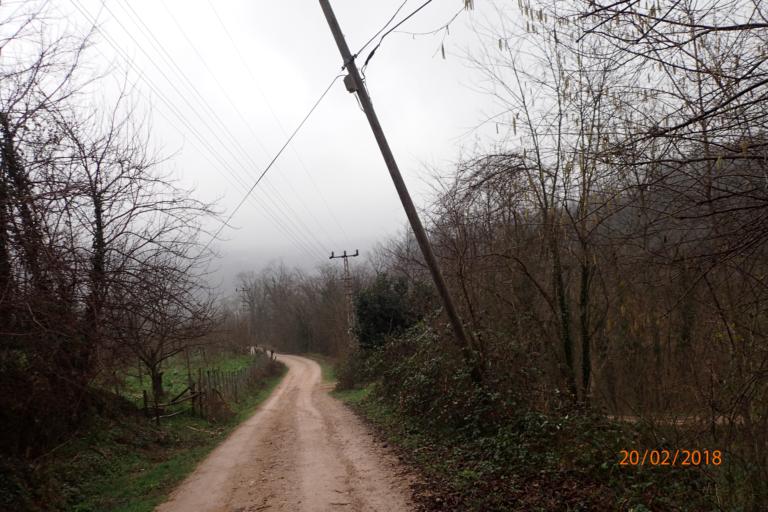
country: TR
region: Ordu
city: Camas
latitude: 40.9471
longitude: 37.5258
